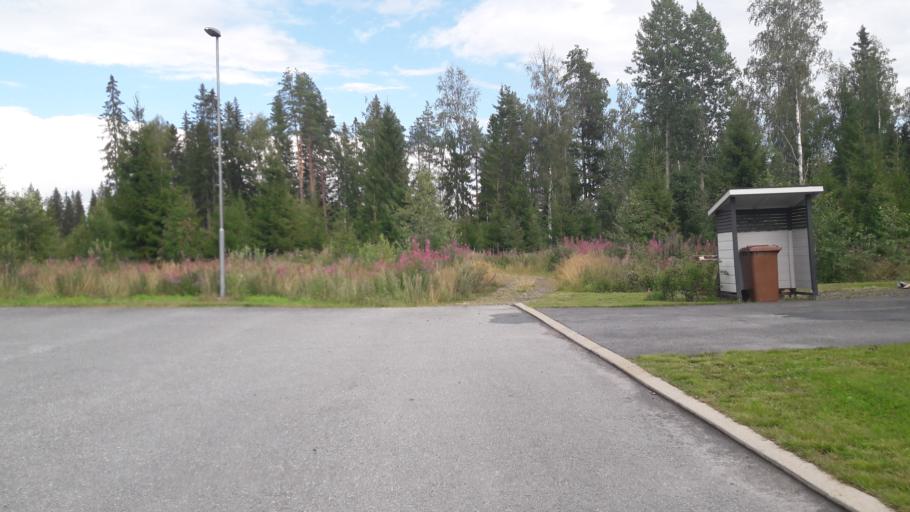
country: FI
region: North Karelia
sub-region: Joensuu
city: Joensuu
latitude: 62.5737
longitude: 29.8293
